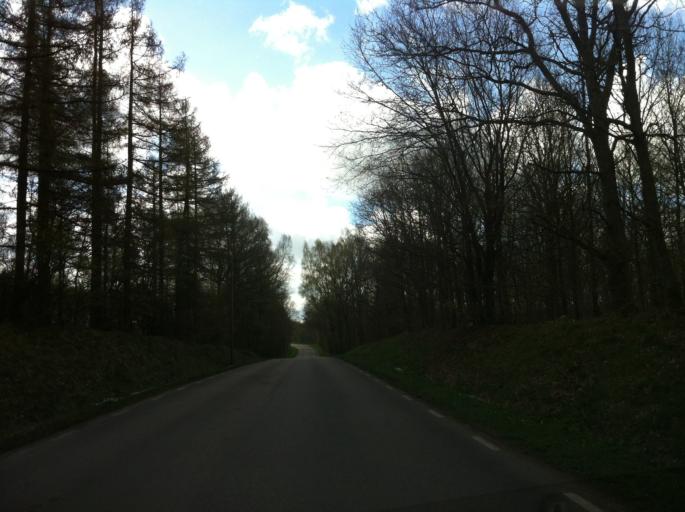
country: SE
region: Skane
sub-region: Horby Kommun
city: Hoerby
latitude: 55.8914
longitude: 13.6149
